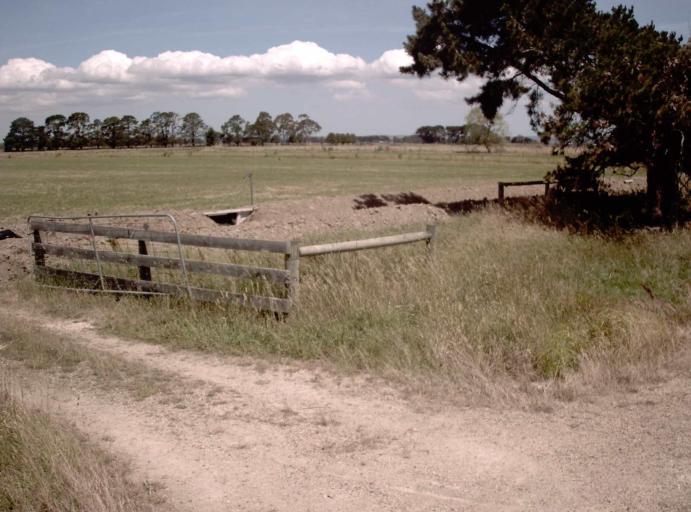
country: AU
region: Victoria
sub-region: Wellington
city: Heyfield
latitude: -38.0605
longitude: 146.8729
